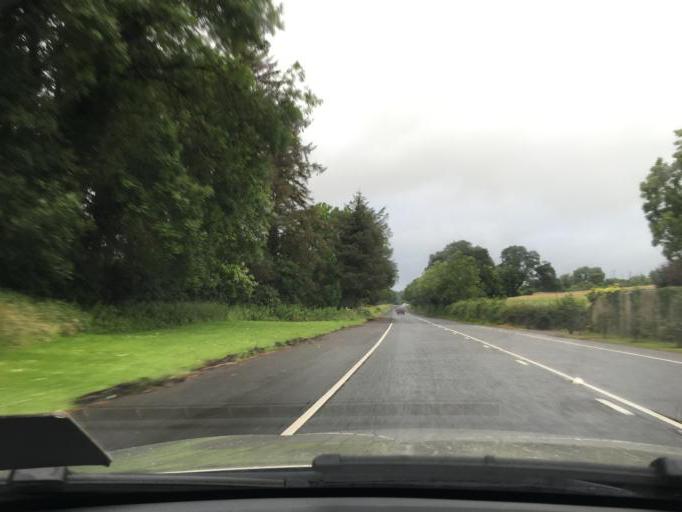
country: GB
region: Northern Ireland
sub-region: Fermanagh District
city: Enniskillen
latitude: 54.3721
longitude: -7.6326
